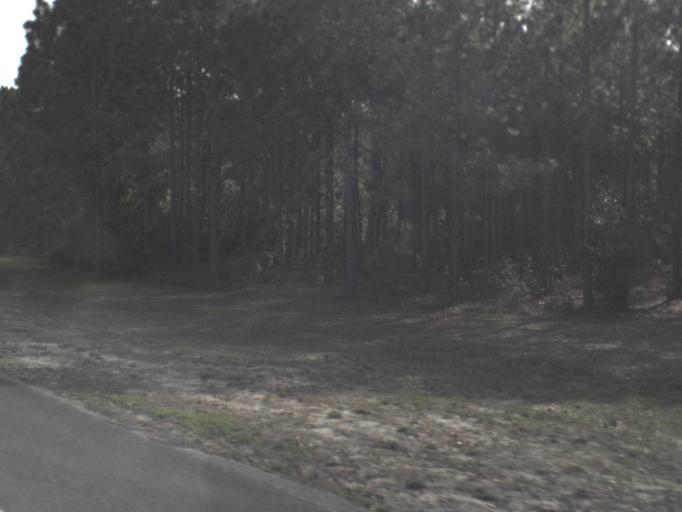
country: US
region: Florida
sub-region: Bay County
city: Tyndall Air Force Base
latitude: 30.0932
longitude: -85.6116
